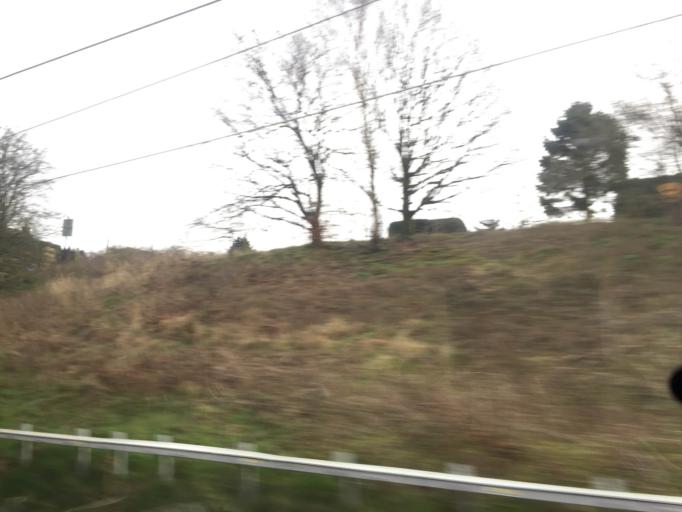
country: GB
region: England
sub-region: Lancashire
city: Coppull
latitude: 53.6343
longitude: -2.6637
